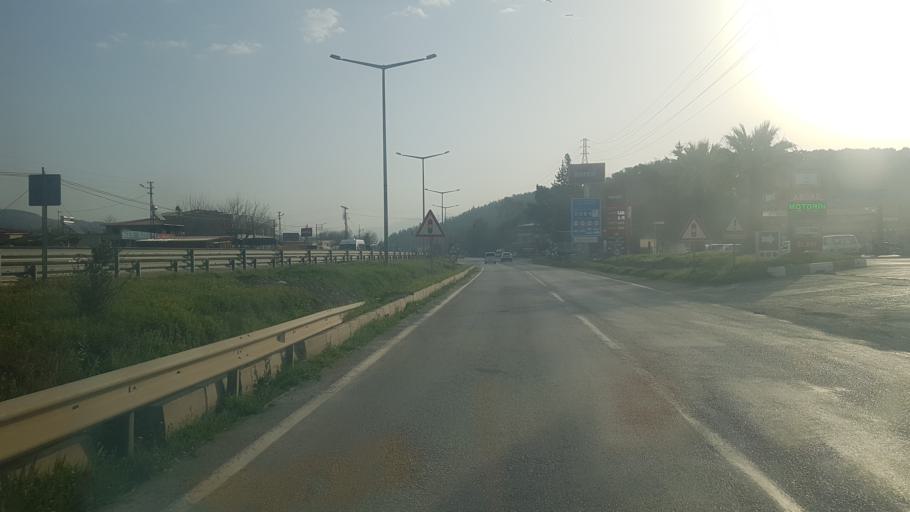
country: TR
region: Osmaniye
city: Toprakkale
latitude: 37.0524
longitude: 36.1543
